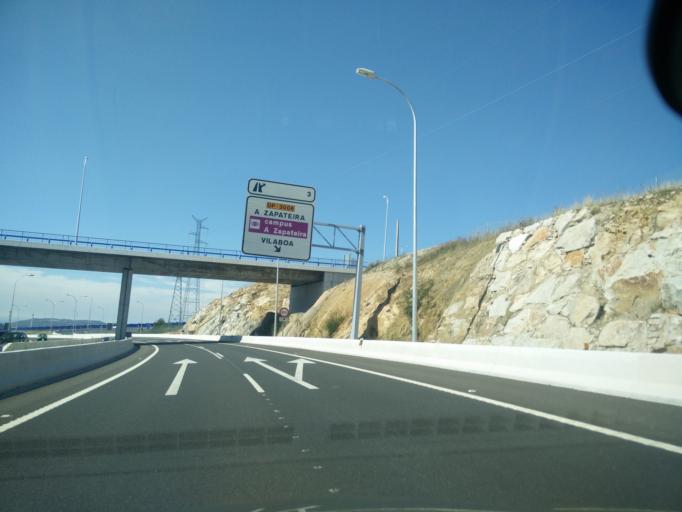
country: ES
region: Galicia
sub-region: Provincia da Coruna
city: Culleredo
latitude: 43.3222
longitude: -8.4091
